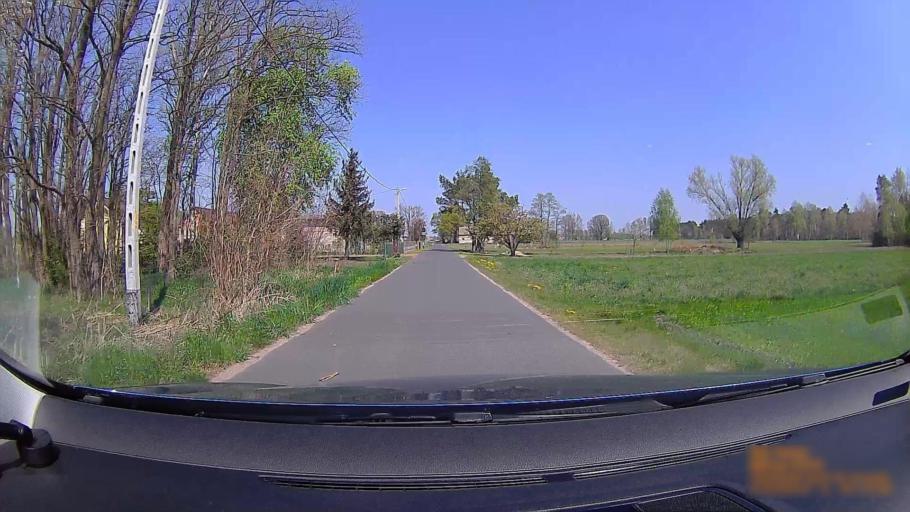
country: PL
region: Greater Poland Voivodeship
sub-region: Powiat koninski
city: Rychwal
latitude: 52.0984
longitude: 18.1843
